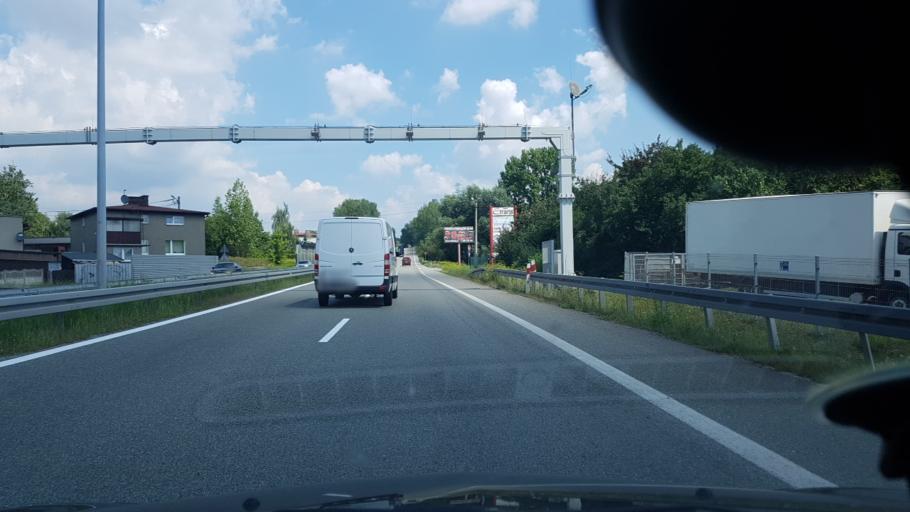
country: PL
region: Silesian Voivodeship
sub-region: Powiat mikolowski
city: Laziska Gorne
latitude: 50.1378
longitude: 18.8346
